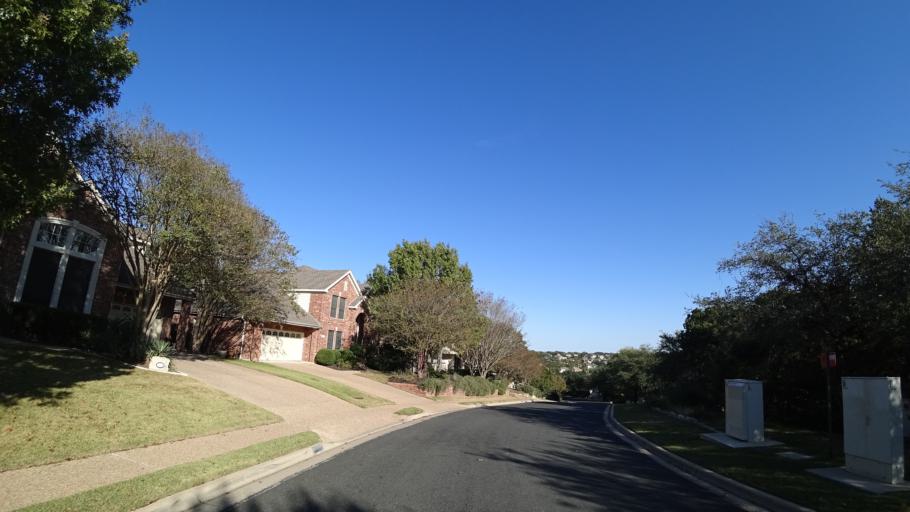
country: US
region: Texas
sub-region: Williamson County
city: Jollyville
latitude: 30.4131
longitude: -97.7786
